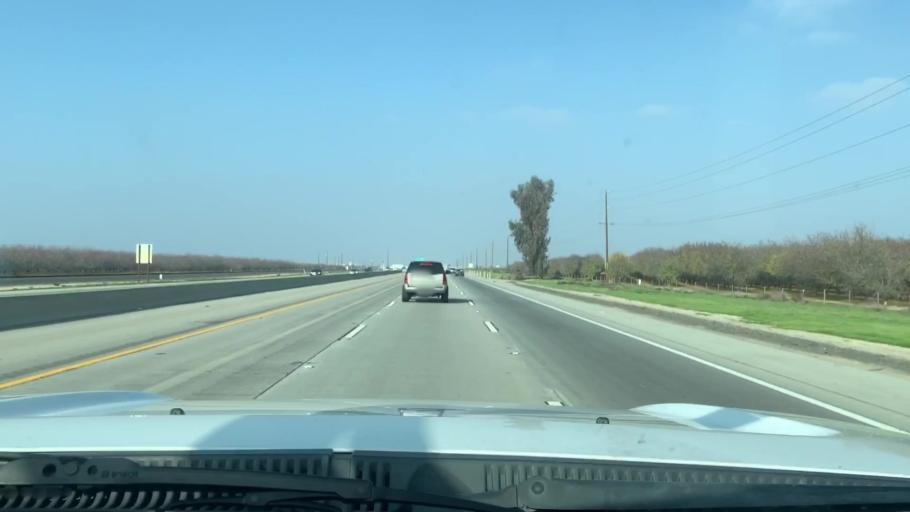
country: US
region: California
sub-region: Kern County
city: Shafter
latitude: 35.5401
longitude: -119.1937
